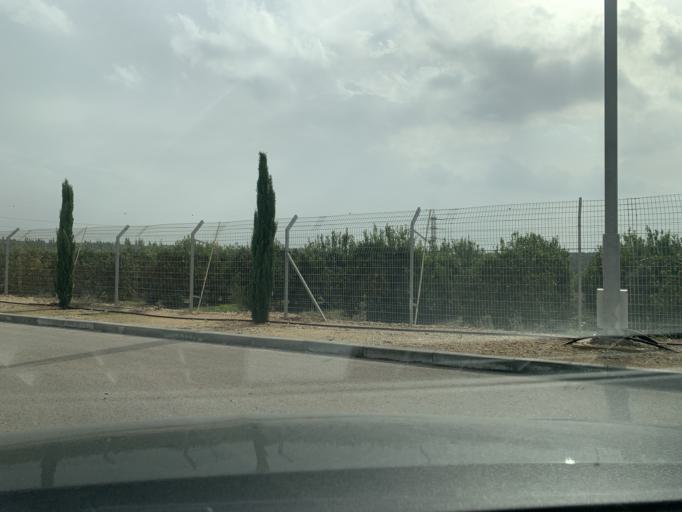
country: IL
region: Central District
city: Tirah
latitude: 32.2151
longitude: 34.9349
